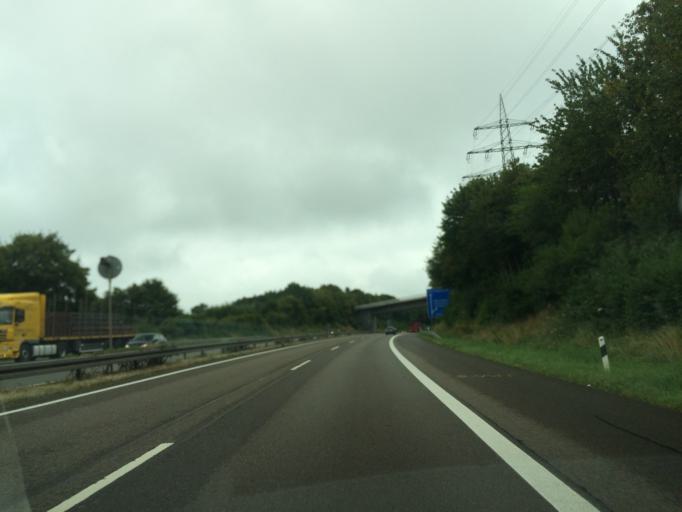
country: DE
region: Saarland
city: Merchweiler
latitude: 49.3485
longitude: 7.0393
